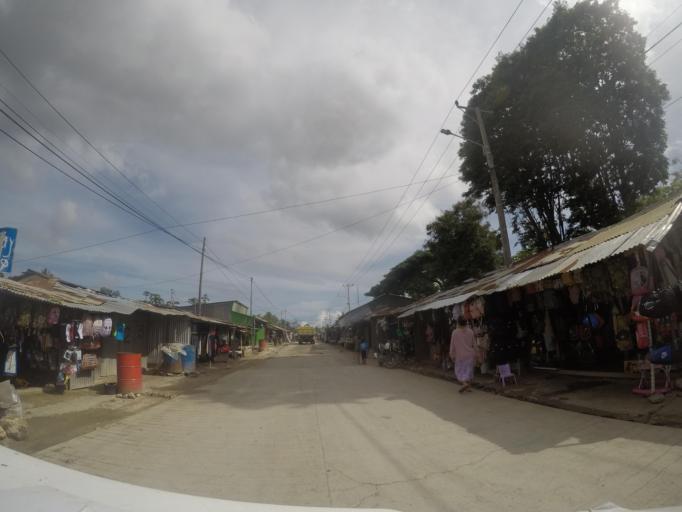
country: TL
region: Baucau
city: Baucau
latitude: -8.4803
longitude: 126.4526
